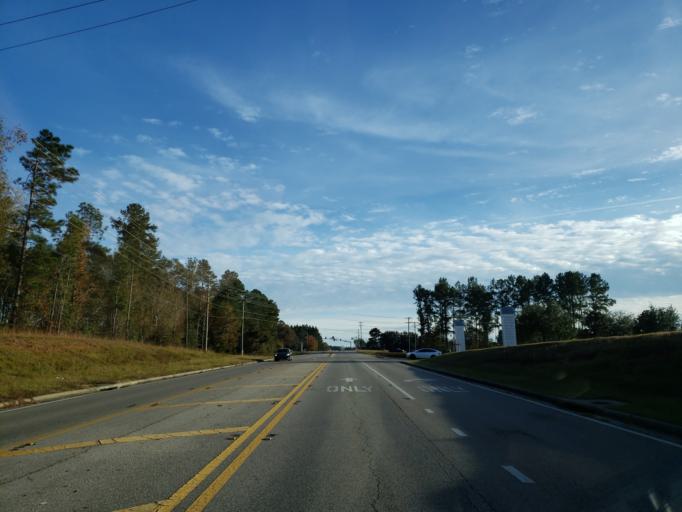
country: US
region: Mississippi
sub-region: Lamar County
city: West Hattiesburg
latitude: 31.2861
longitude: -89.4692
